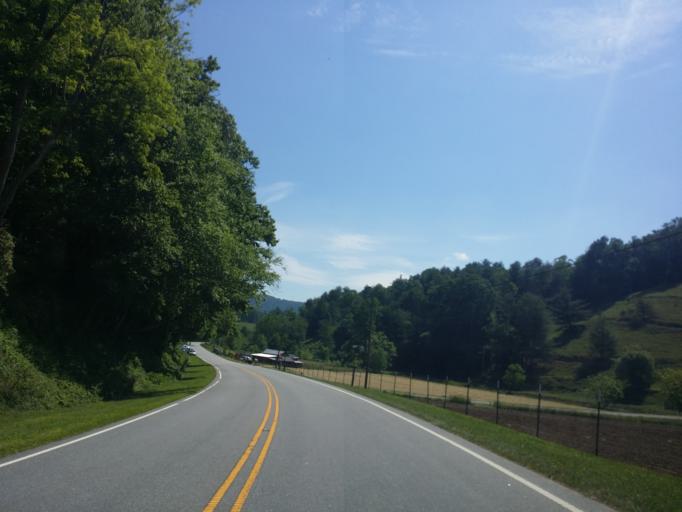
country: US
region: North Carolina
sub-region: Madison County
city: Marshall
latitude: 35.7010
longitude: -82.8026
